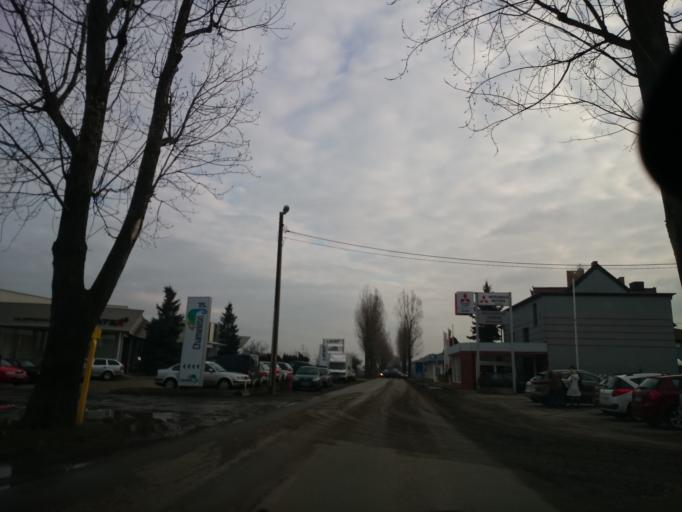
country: PL
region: Opole Voivodeship
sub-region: Powiat opolski
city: Opole
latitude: 50.6542
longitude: 17.9093
